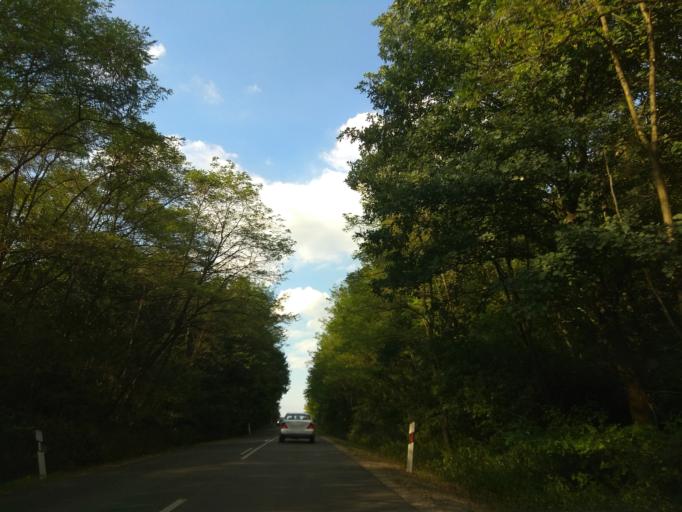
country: HU
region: Borsod-Abauj-Zemplen
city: Harsany
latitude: 47.9835
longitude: 20.7473
